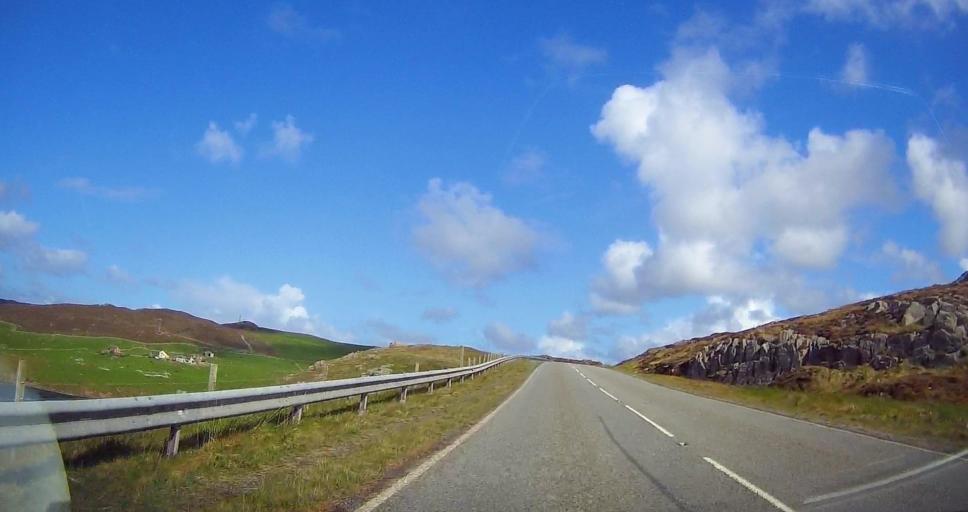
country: GB
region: Scotland
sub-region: Shetland Islands
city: Lerwick
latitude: 60.4168
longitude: -1.3926
